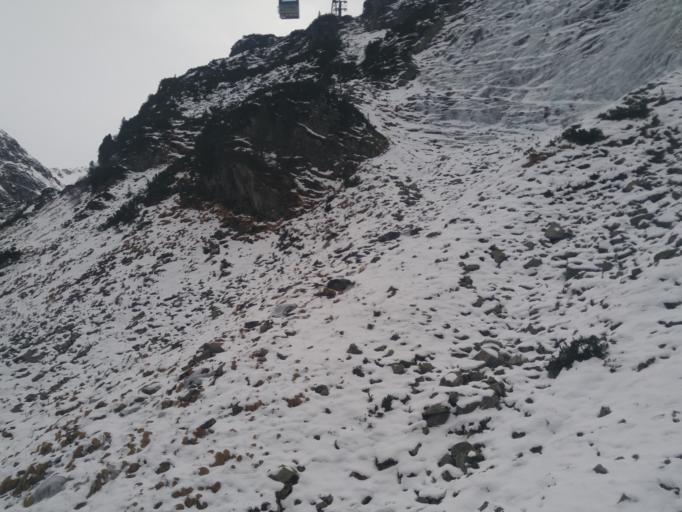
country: AT
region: Salzburg
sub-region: Politischer Bezirk Zell am See
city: Niedernsill
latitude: 47.1532
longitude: 12.6240
